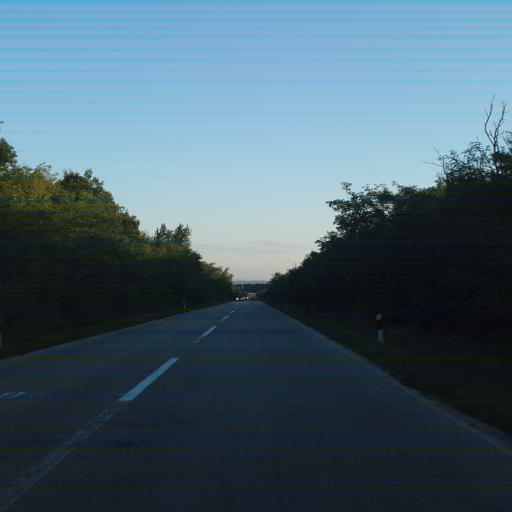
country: RS
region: Central Serbia
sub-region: Borski Okrug
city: Negotin
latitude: 44.1762
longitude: 22.3651
